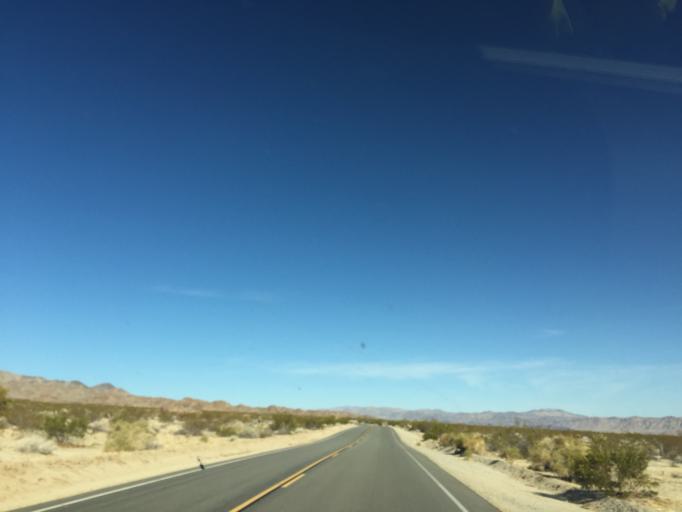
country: US
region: California
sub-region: San Bernardino County
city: Twentynine Palms
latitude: 33.8495
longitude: -115.7816
